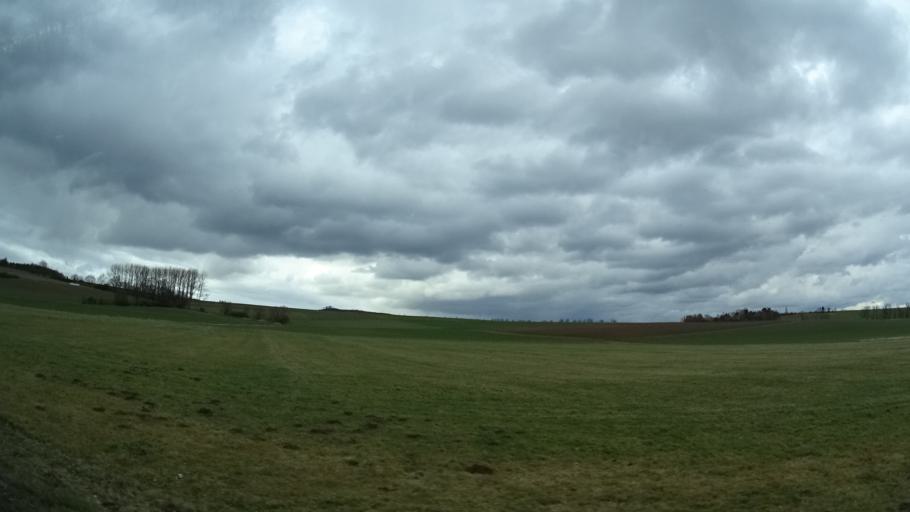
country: DE
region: Hesse
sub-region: Regierungsbezirk Giessen
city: Schlitz
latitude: 50.6635
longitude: 9.5377
